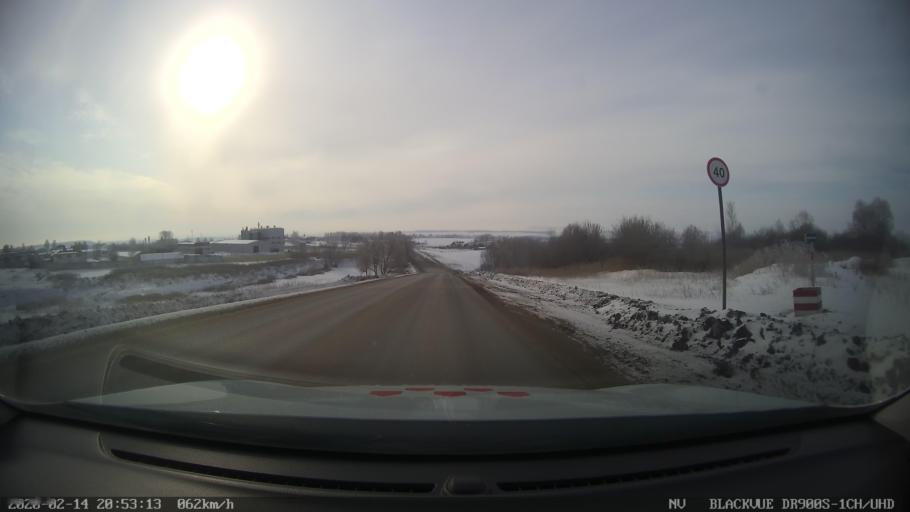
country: RU
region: Tatarstan
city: Kuybyshevskiy Zaton
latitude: 55.1969
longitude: 49.2479
